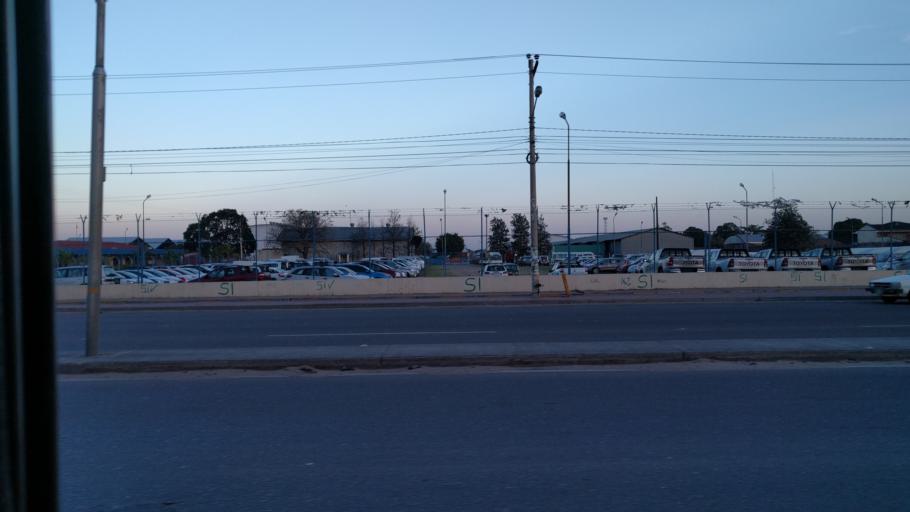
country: BO
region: Santa Cruz
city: Santa Cruz de la Sierra
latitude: -17.7738
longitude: -63.1318
